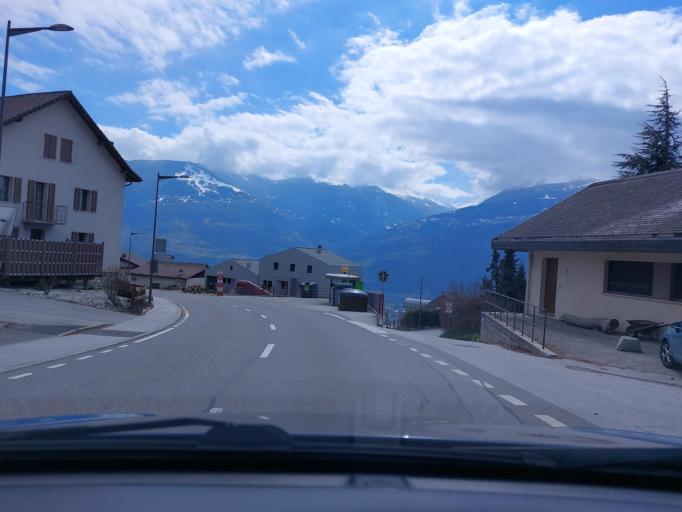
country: CH
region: Valais
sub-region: Conthey District
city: Vetroz
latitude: 46.2379
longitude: 7.2924
